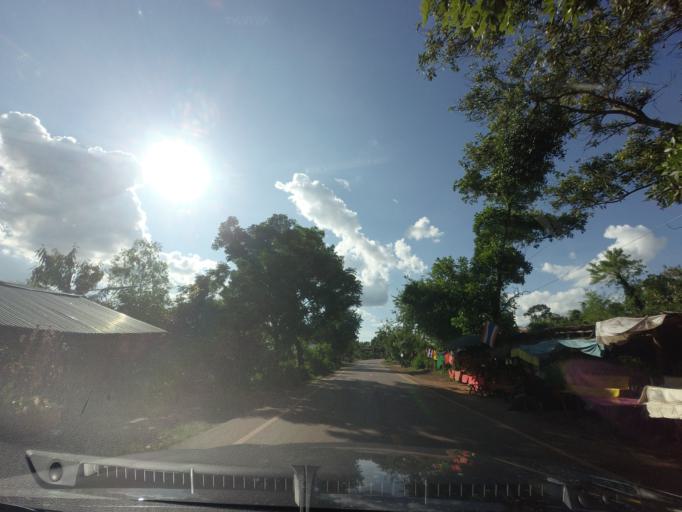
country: TH
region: Changwat Udon Thani
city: Ban Dung
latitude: 17.7443
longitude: 103.3369
